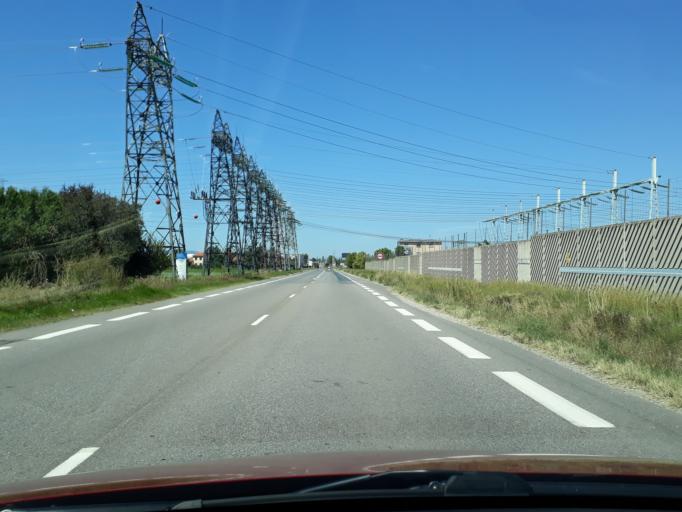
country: FR
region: Rhone-Alpes
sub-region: Departement du Rhone
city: Toussieu
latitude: 45.6728
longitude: 4.9756
